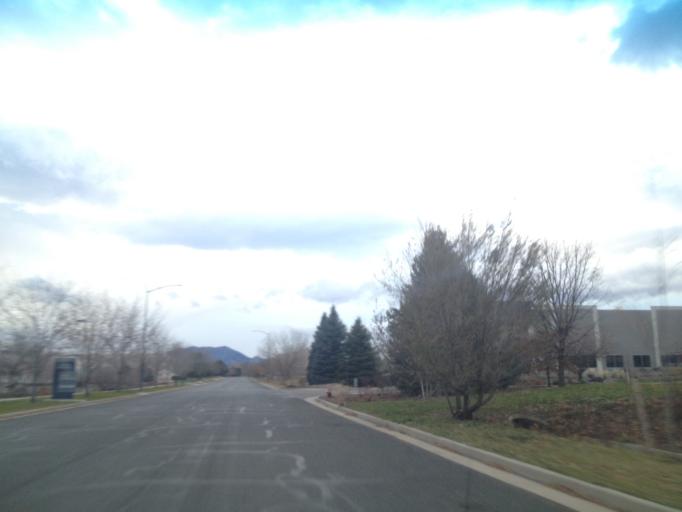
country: US
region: Colorado
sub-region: Boulder County
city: Louisville
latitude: 39.9651
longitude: -105.1166
